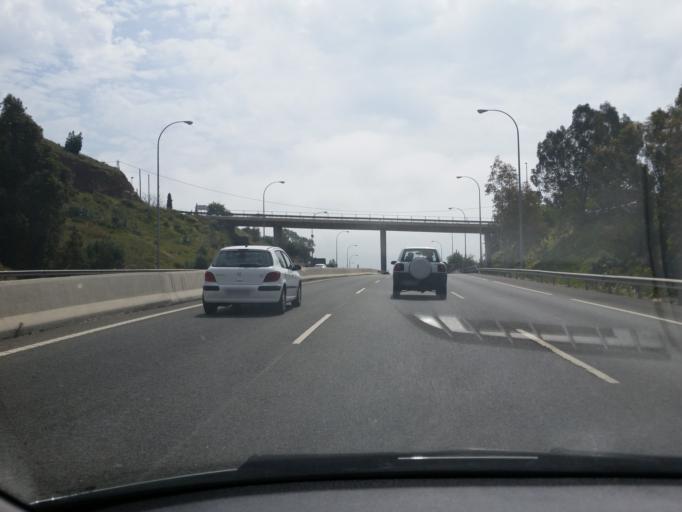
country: ES
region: Andalusia
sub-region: Provincia de Malaga
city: Malaga
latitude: 36.7473
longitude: -4.4092
